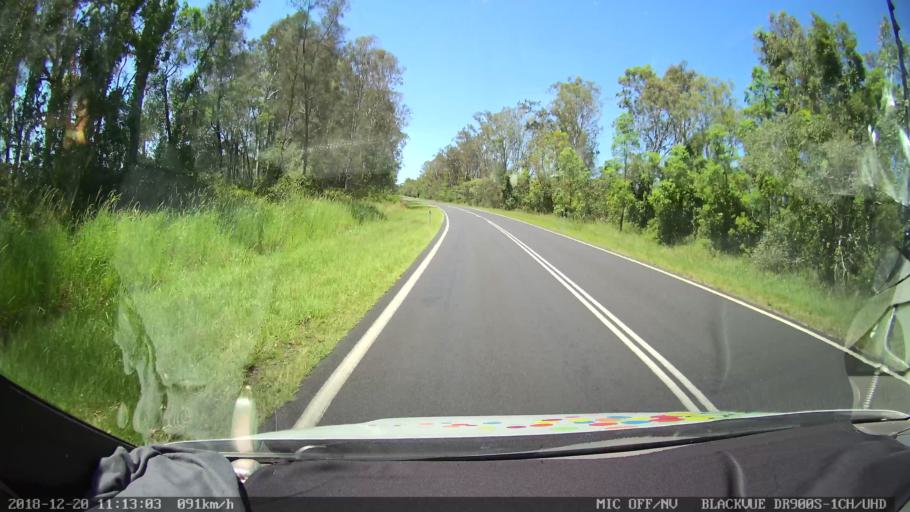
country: AU
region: New South Wales
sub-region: Richmond Valley
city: Casino
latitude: -28.9824
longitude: 153.0093
